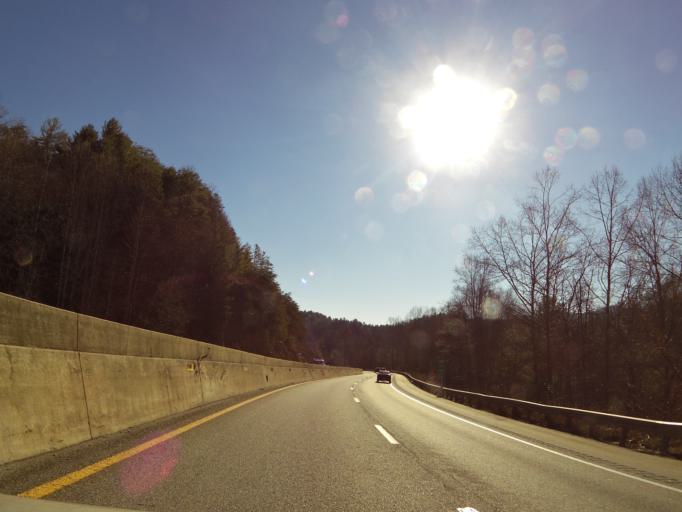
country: US
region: North Carolina
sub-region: Haywood County
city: Cove Creek
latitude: 35.6934
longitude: -83.0380
